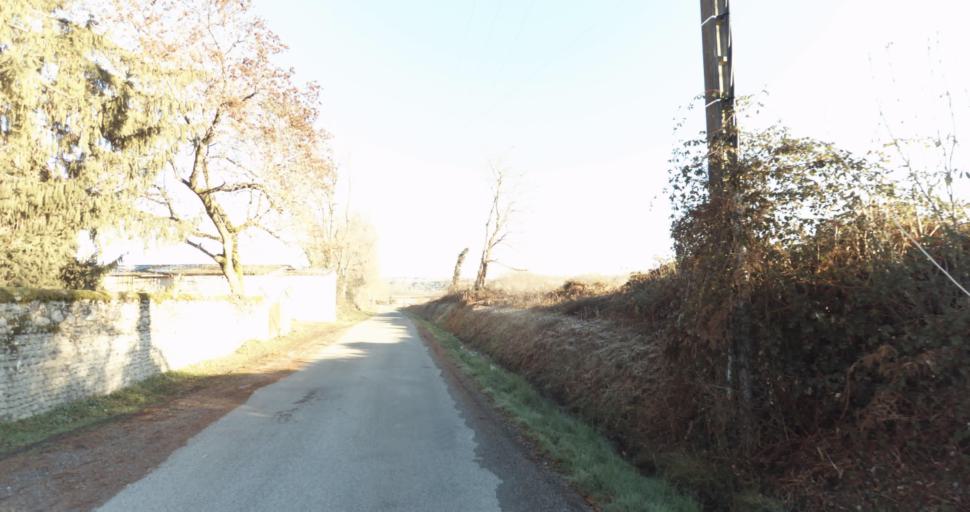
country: FR
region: Aquitaine
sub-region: Departement des Pyrenees-Atlantiques
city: Ousse
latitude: 43.3080
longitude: -0.2617
